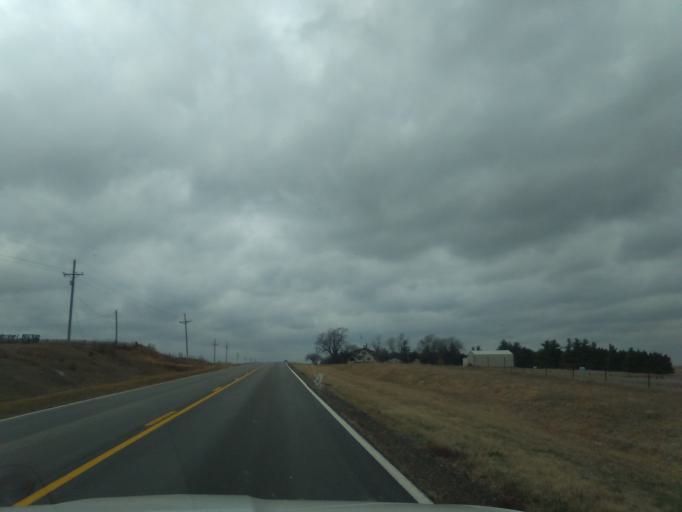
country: US
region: Kansas
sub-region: Nemaha County
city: Sabetha
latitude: 40.0587
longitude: -95.9007
